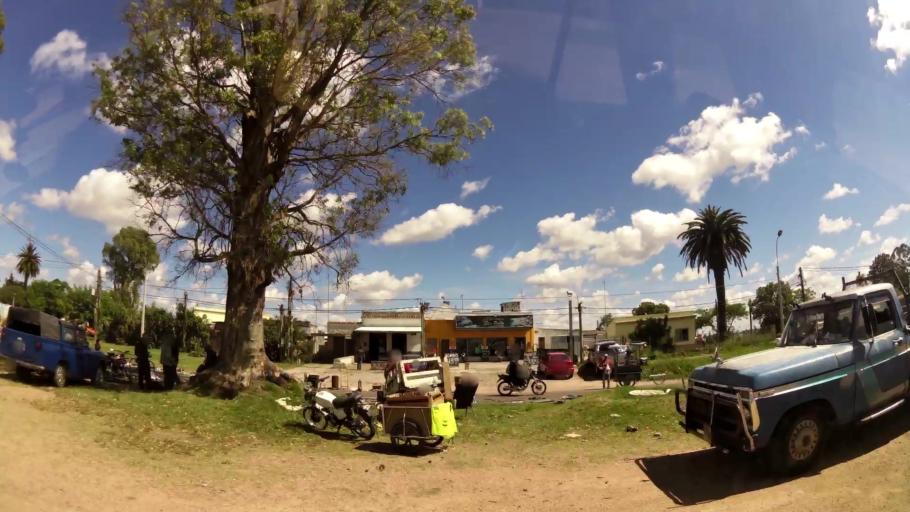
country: UY
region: Canelones
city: Paso de Carrasco
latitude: -34.8382
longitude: -56.1330
